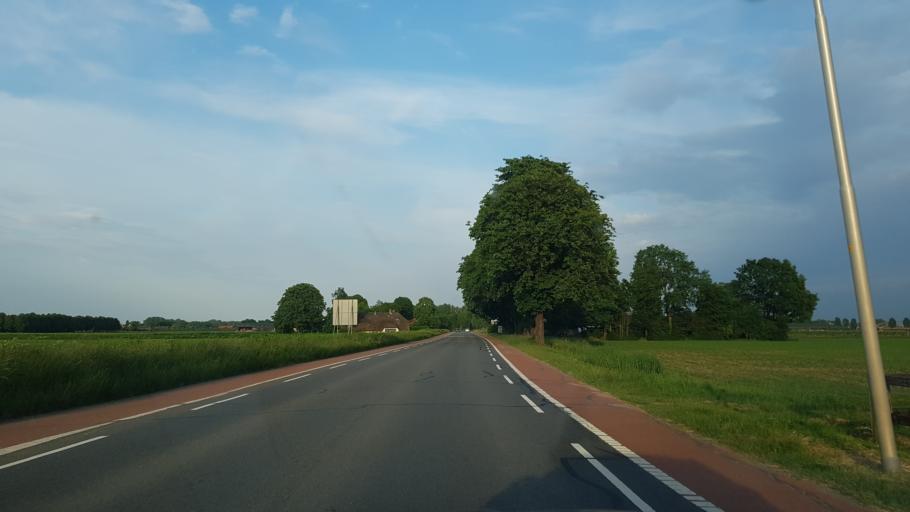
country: NL
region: Gelderland
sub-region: Gemeente Wijchen
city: Bergharen
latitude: 51.8825
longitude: 5.6486
